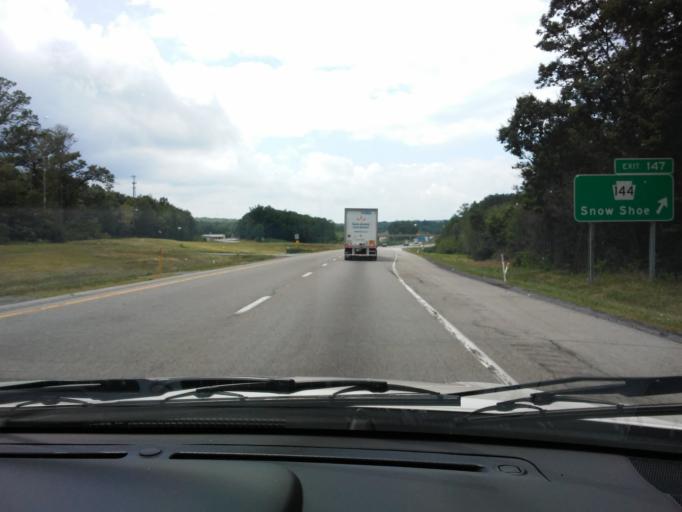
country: US
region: Pennsylvania
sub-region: Centre County
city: Milesburg
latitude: 41.0243
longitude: -77.9277
